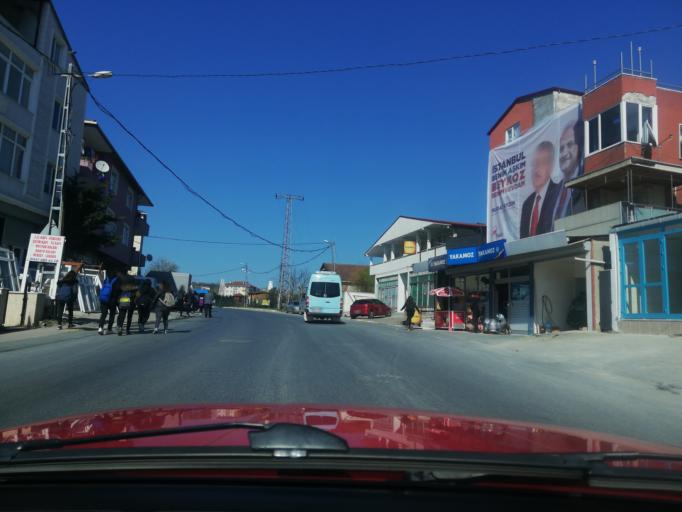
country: TR
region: Istanbul
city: Umraniye
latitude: 41.0909
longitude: 29.1412
